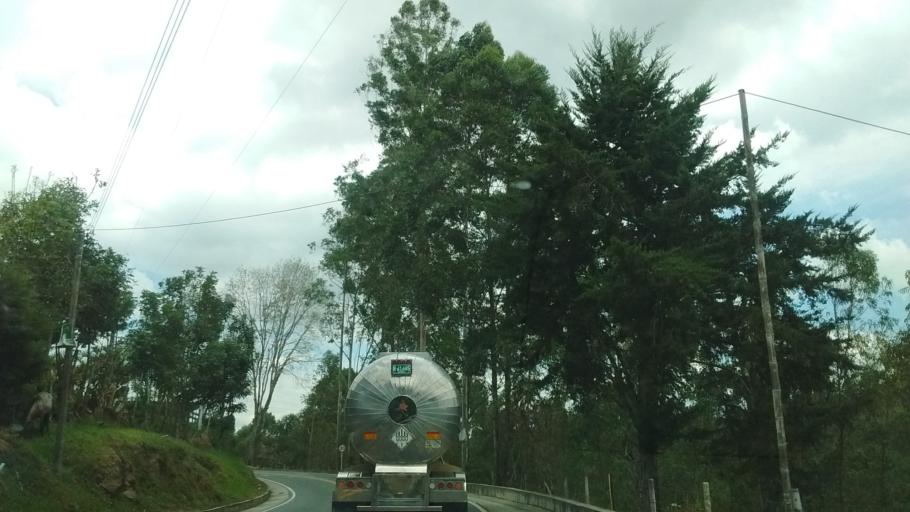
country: CO
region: Cauca
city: Rosas
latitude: 2.3066
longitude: -76.6972
